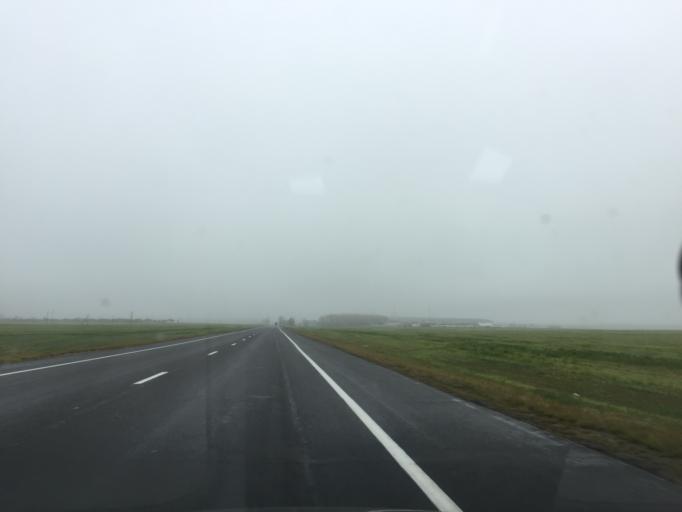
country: BY
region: Mogilev
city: Shklow
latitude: 54.2457
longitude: 30.4510
